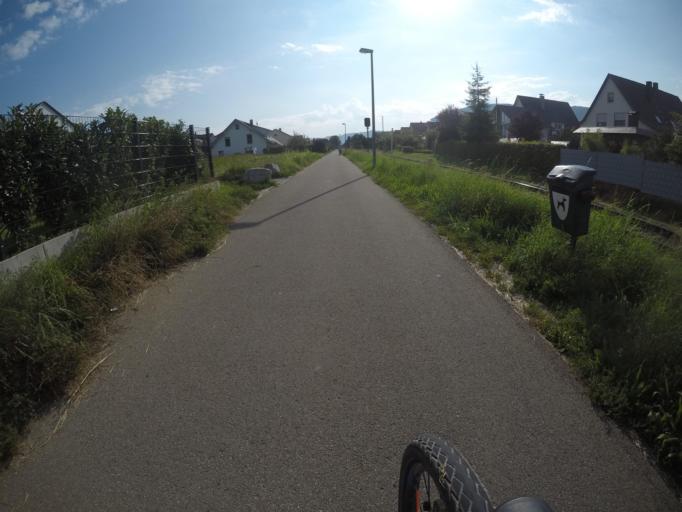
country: DE
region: Baden-Wuerttemberg
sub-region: Tuebingen Region
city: Metzingen
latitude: 48.5334
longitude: 9.3023
